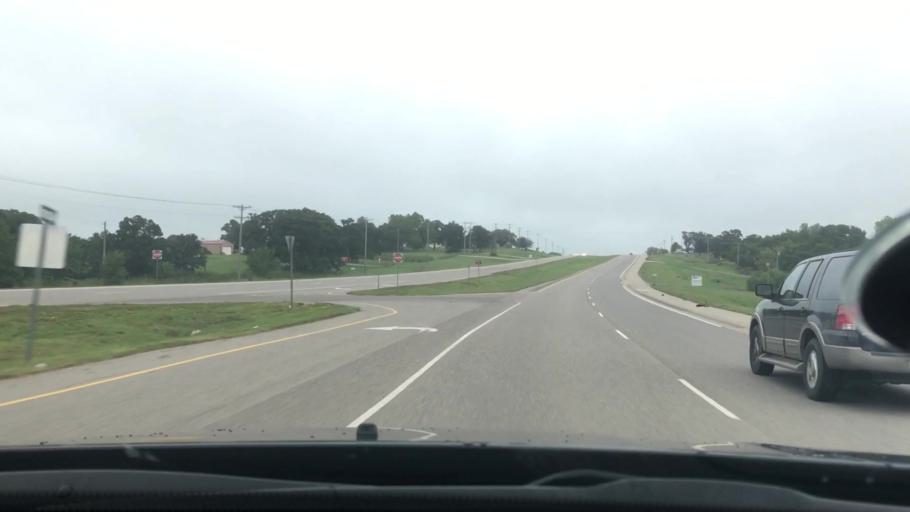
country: US
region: Oklahoma
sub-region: Seminole County
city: Seminole
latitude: 35.3107
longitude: -96.6713
